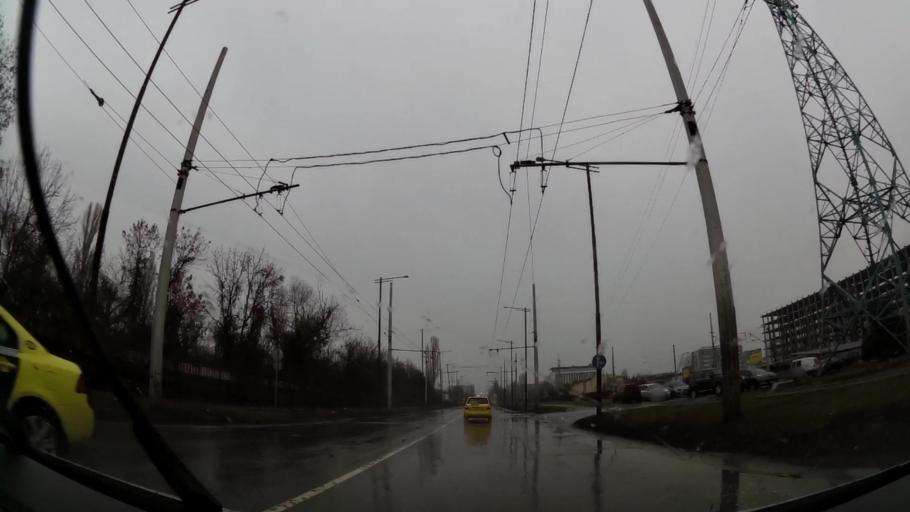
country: BG
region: Sofia-Capital
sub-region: Stolichna Obshtina
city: Sofia
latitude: 42.6736
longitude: 23.3840
